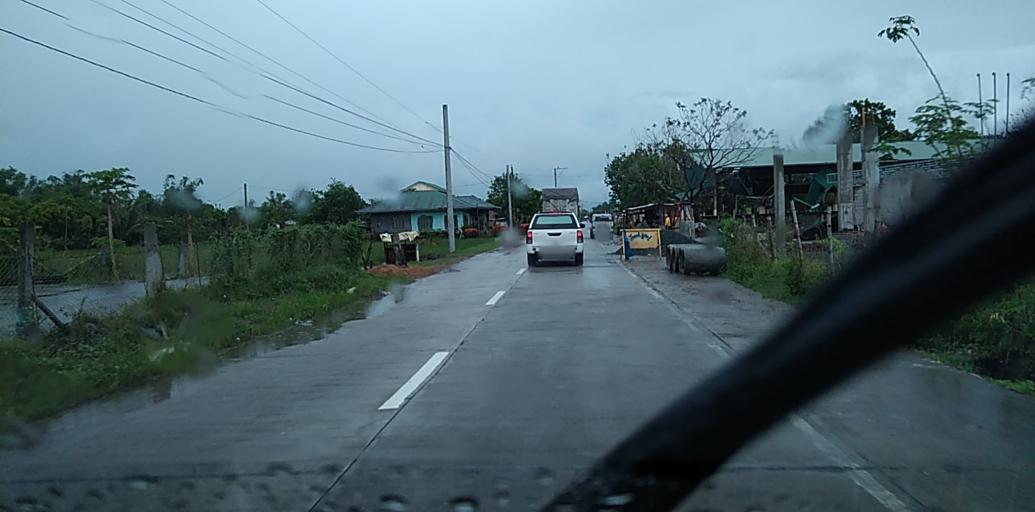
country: PH
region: Central Luzon
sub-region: Province of Pampanga
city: Salapungan
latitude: 15.1346
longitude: 120.9301
